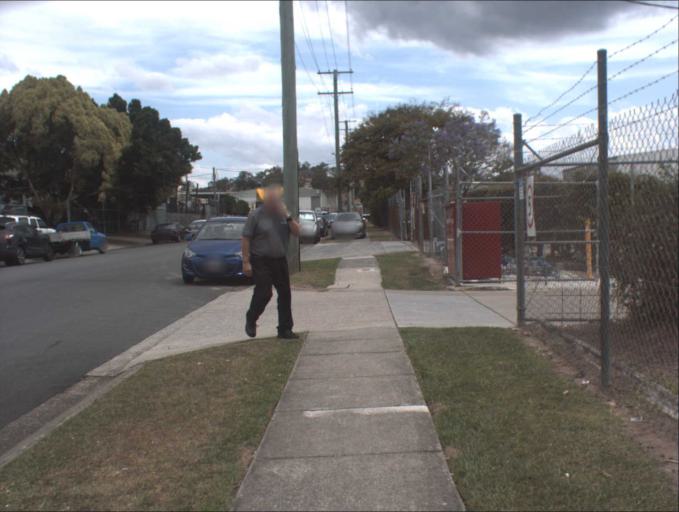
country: AU
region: Queensland
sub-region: Logan
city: Beenleigh
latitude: -27.7110
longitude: 153.1851
